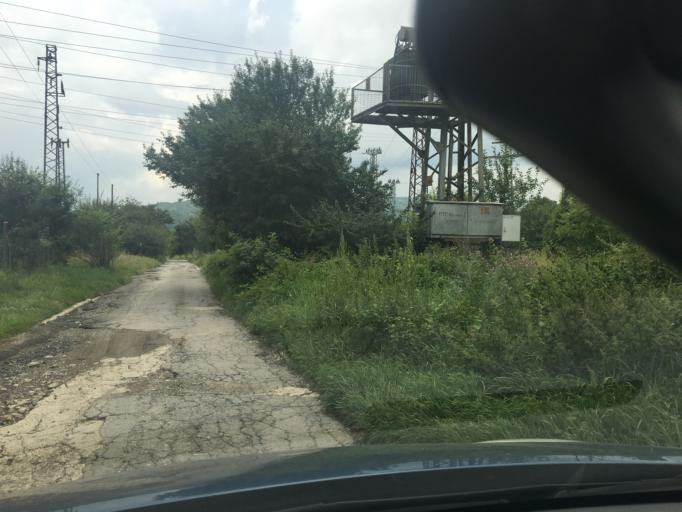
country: BG
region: Sofia-Capital
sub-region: Stolichna Obshtina
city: Sofia
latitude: 42.5840
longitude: 23.3700
